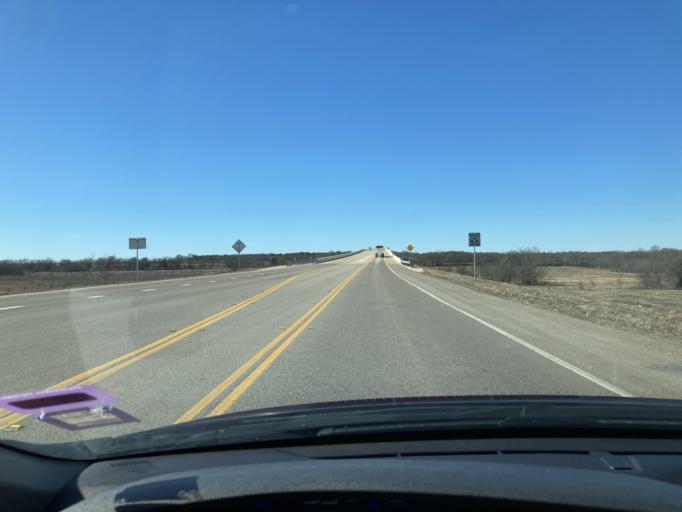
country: US
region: Texas
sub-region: Navarro County
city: Corsicana
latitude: 32.0416
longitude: -96.4489
